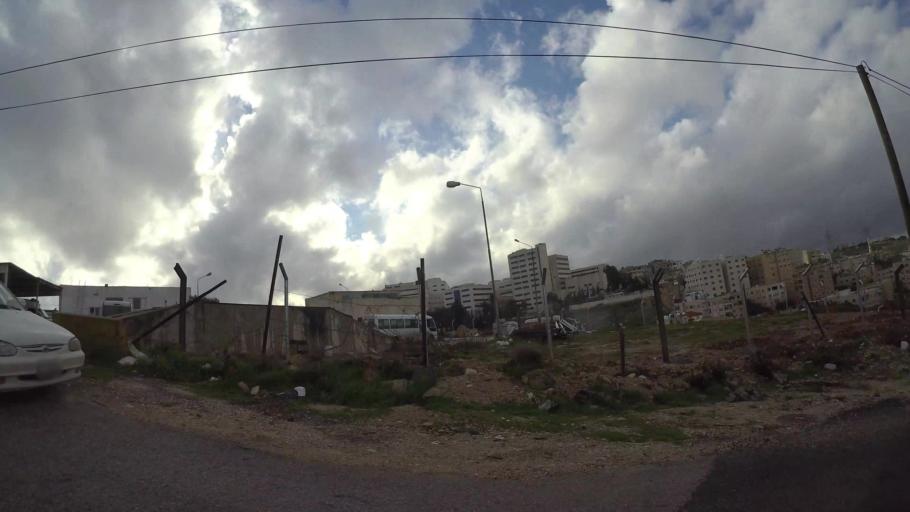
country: JO
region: Amman
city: Amman
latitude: 32.0001
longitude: 35.9231
